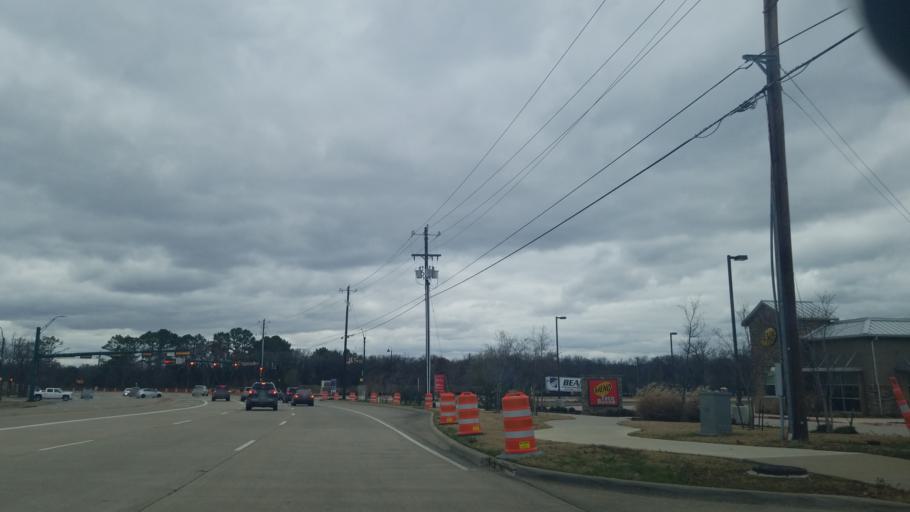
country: US
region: Texas
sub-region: Denton County
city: Flower Mound
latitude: 33.0464
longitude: -97.0693
